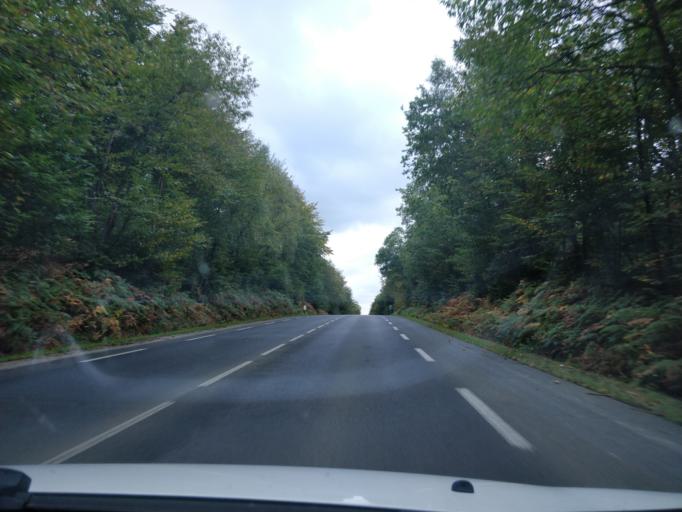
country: FR
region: Lower Normandy
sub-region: Departement du Calvados
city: Saint-Sever-Calvados
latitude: 48.8329
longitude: -1.0692
